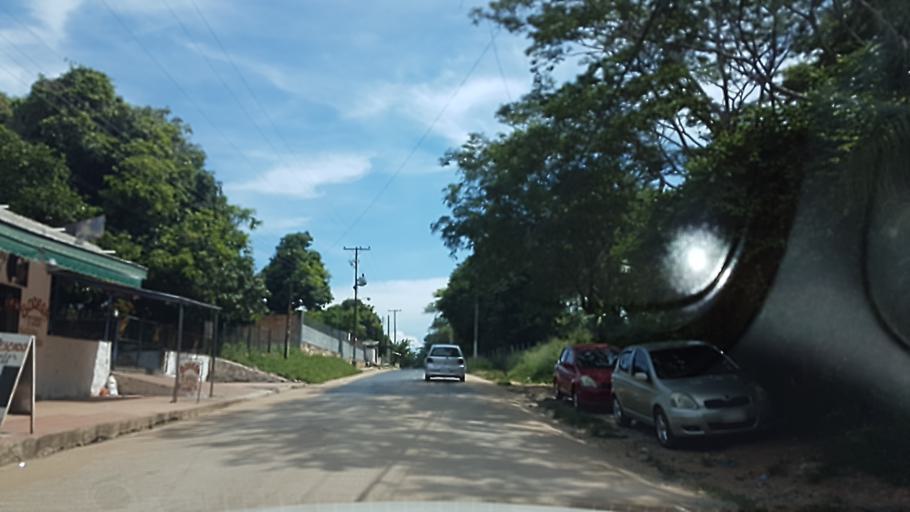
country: PY
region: Central
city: Colonia Mariano Roque Alonso
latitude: -25.1860
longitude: -57.5404
